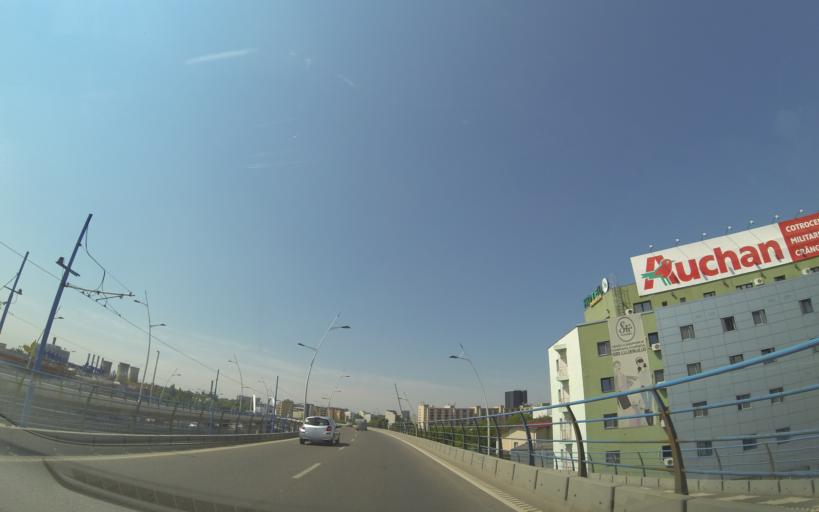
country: RO
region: Bucuresti
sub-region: Municipiul Bucuresti
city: Bucuresti
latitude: 44.4464
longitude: 26.0618
